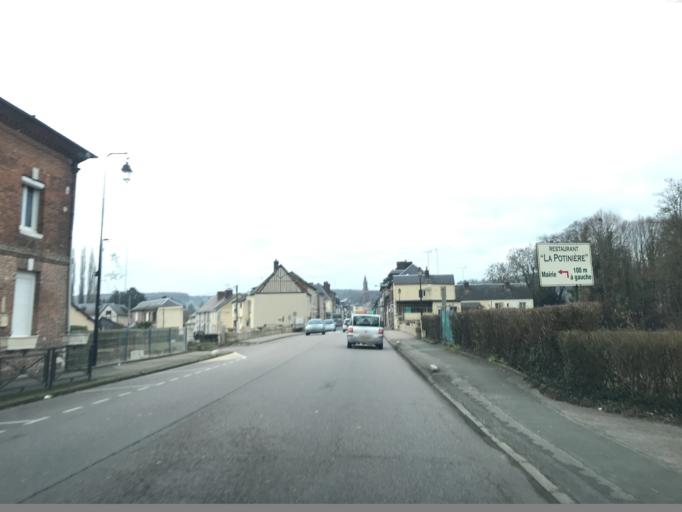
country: FR
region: Haute-Normandie
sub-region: Departement de l'Eure
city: Fleury-sur-Andelle
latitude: 49.3586
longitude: 1.3588
